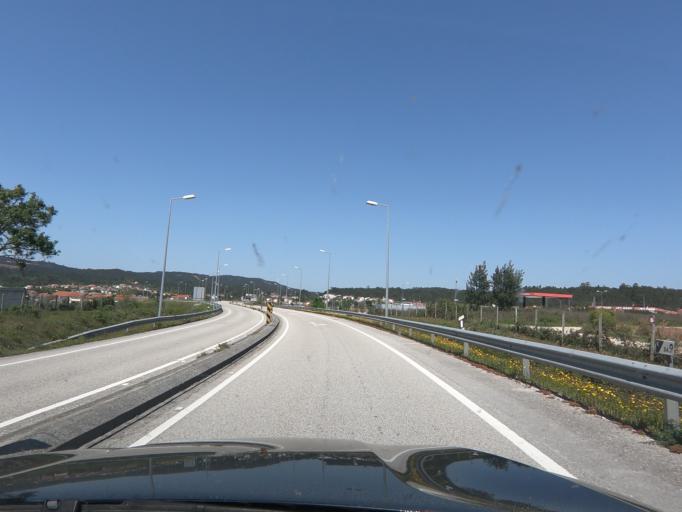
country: PT
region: Coimbra
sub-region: Miranda do Corvo
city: Miranda do Corvo
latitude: 40.0845
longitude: -8.3245
